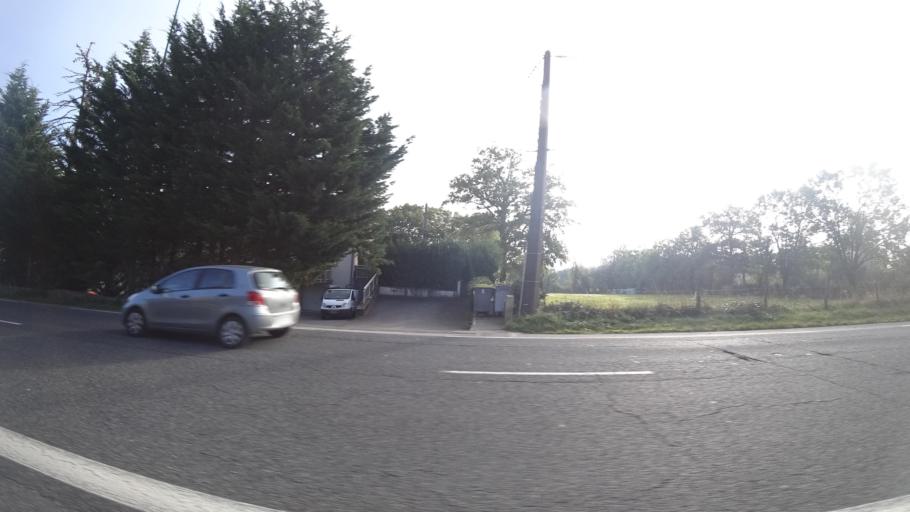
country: FR
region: Midi-Pyrenees
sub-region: Departement de l'Aveyron
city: Luc-la-Primaube
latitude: 44.3062
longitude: 2.5572
